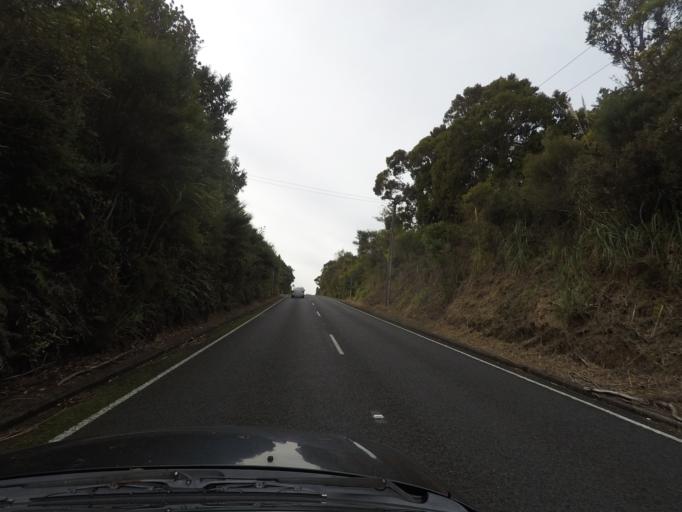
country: NZ
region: Auckland
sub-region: Auckland
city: Titirangi
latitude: -36.9473
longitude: 174.5243
